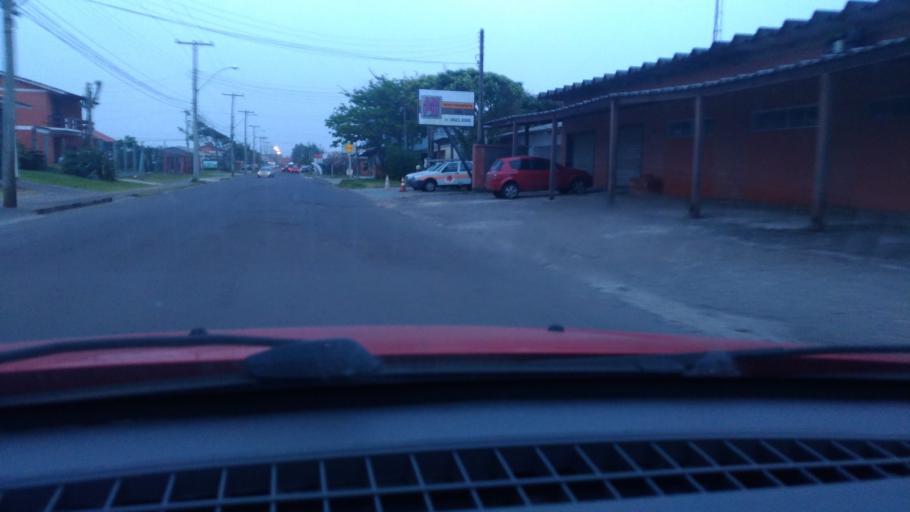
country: BR
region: Rio Grande do Sul
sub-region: Capao Da Canoa
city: Capao da Canoa
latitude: -29.8507
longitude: -50.0647
